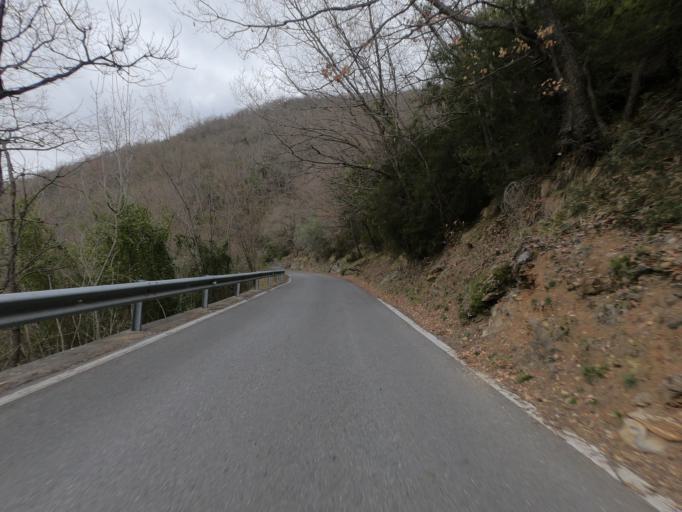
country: IT
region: Liguria
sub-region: Provincia di Savona
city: Testico
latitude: 44.0282
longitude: 8.0155
